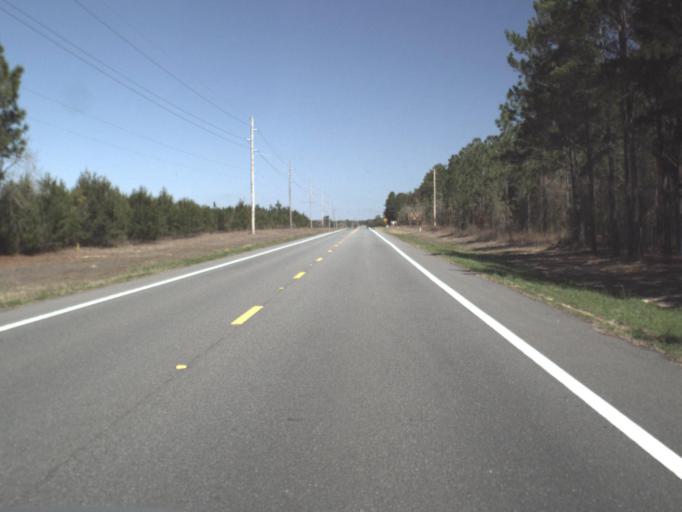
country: US
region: Florida
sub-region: Gadsden County
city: Quincy
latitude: 30.4389
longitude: -84.6467
